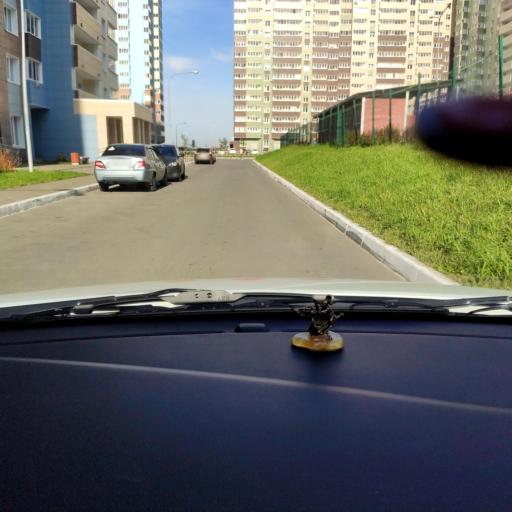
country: RU
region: Tatarstan
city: Osinovo
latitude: 55.8648
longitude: 48.8743
